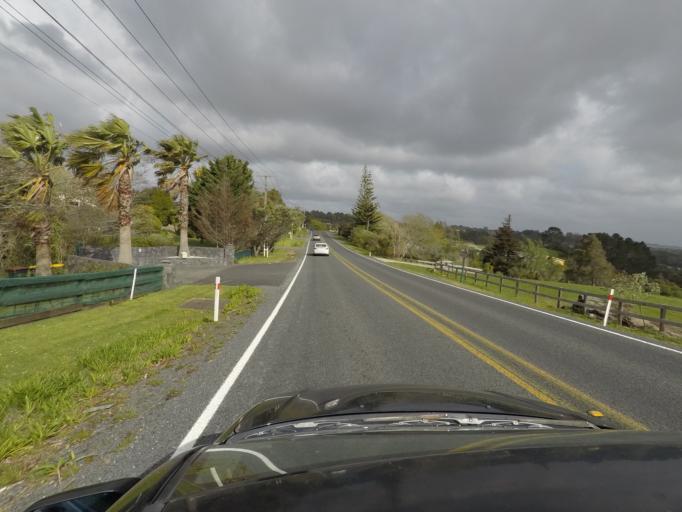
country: NZ
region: Auckland
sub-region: Auckland
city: Pakuranga
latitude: -36.9339
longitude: 174.9385
